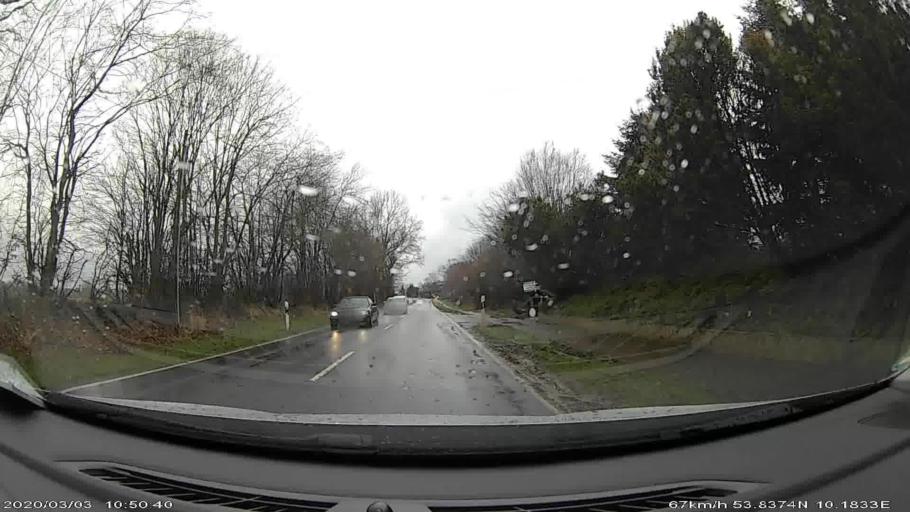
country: DE
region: Schleswig-Holstein
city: Seth
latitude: 53.8398
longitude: 10.1813
